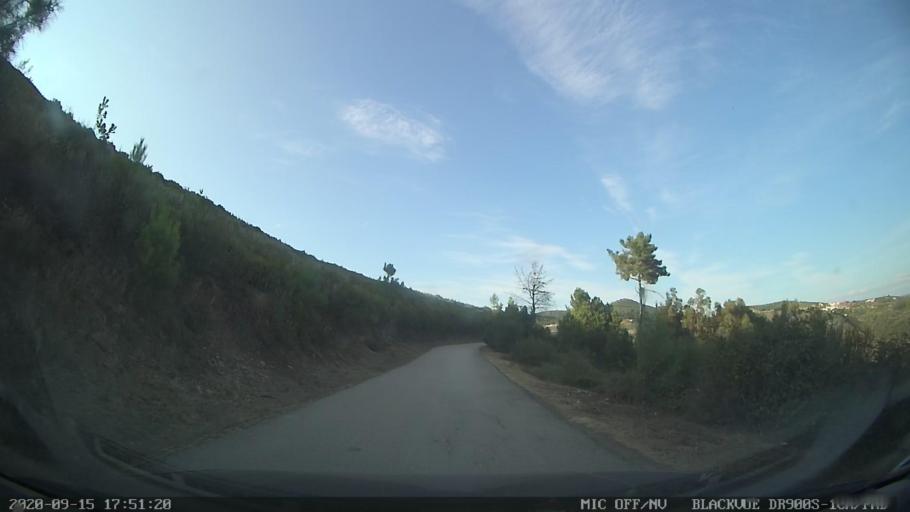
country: PT
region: Vila Real
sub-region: Sabrosa
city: Vilela
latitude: 41.2050
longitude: -7.5823
